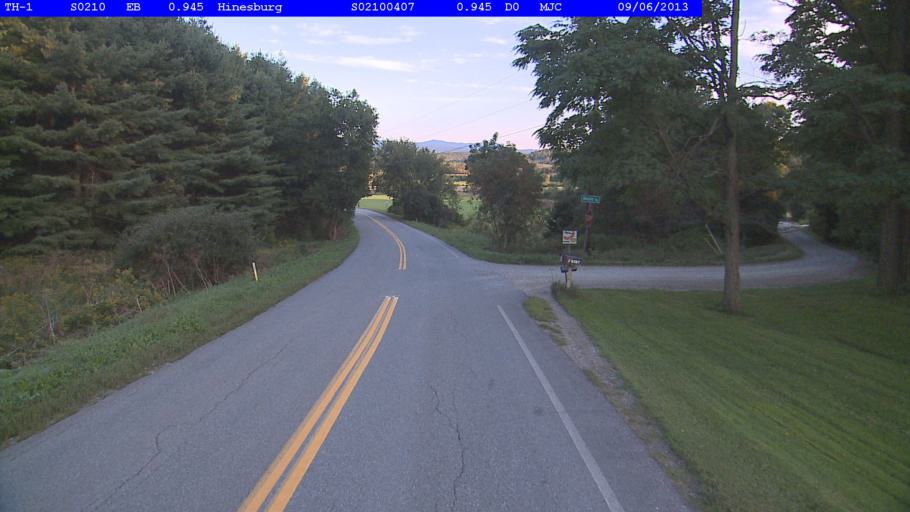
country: US
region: Vermont
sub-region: Chittenden County
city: Hinesburg
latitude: 44.3511
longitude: -73.1518
